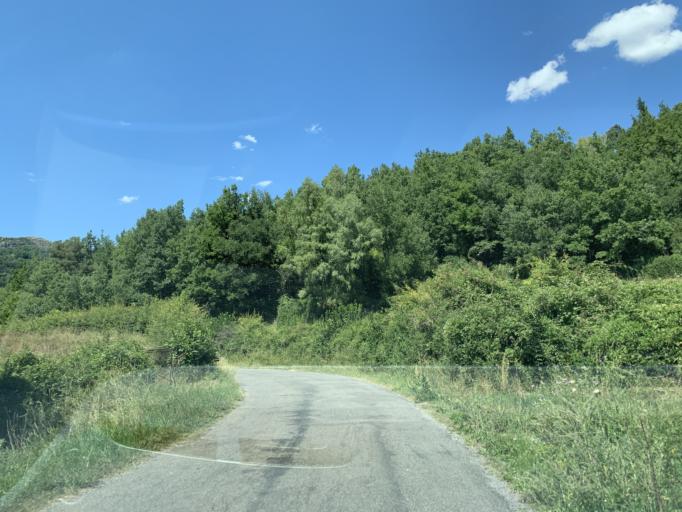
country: ES
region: Aragon
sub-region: Provincia de Huesca
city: Hoz de Jaca
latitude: 42.7055
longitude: -0.3034
